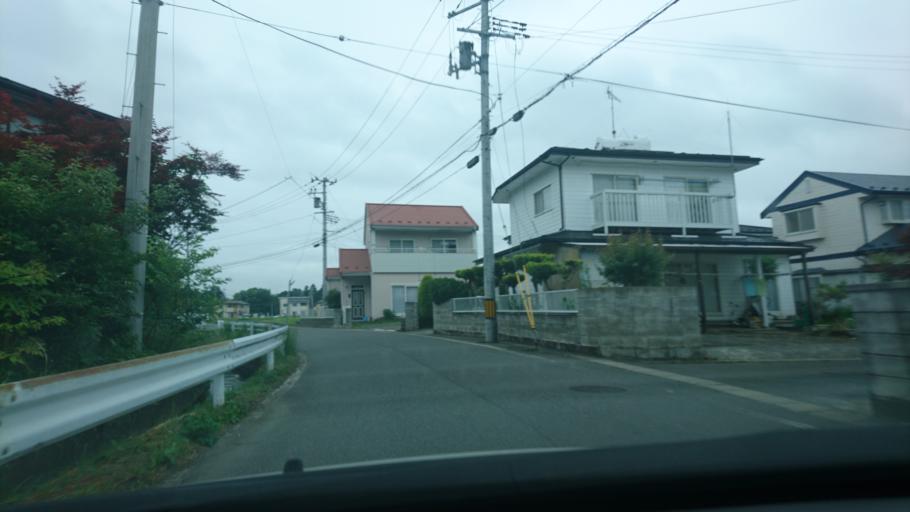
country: JP
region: Iwate
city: Ichinoseki
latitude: 38.9158
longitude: 141.0936
